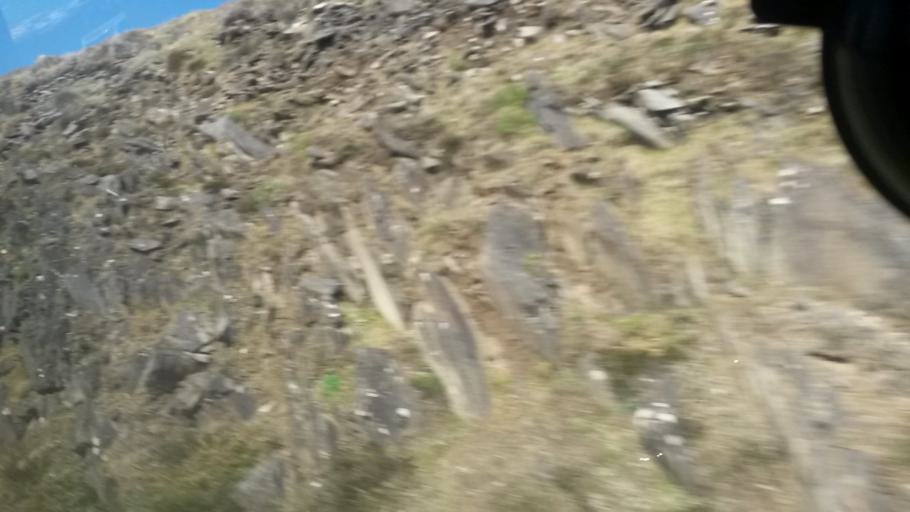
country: IE
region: Munster
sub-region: Ciarrai
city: Dingle
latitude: 52.1020
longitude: -10.4560
